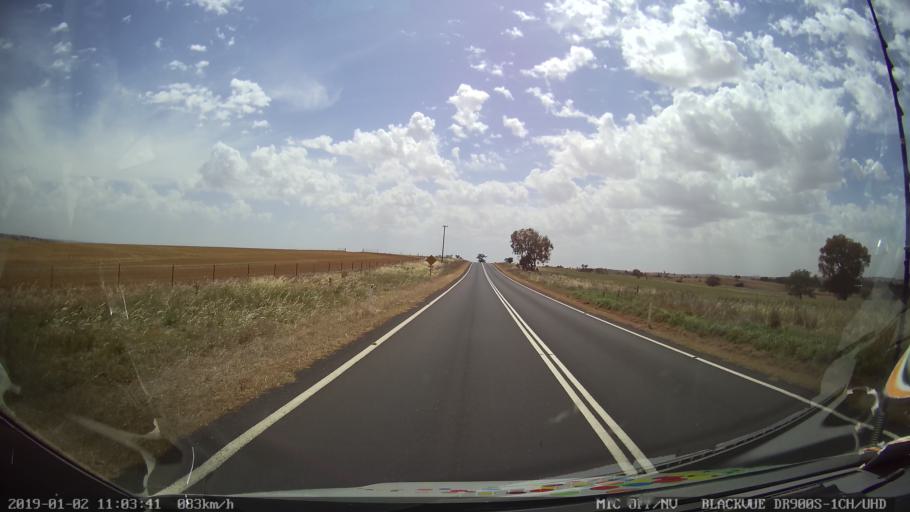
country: AU
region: New South Wales
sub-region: Young
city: Young
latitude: -34.5767
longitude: 148.3414
